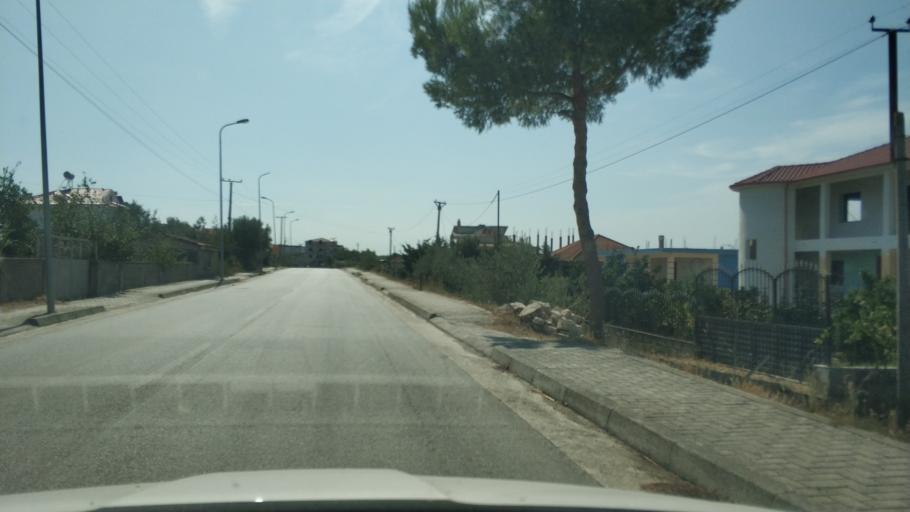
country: AL
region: Fier
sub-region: Rrethi i Lushnjes
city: Divjake
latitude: 40.9799
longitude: 19.5351
